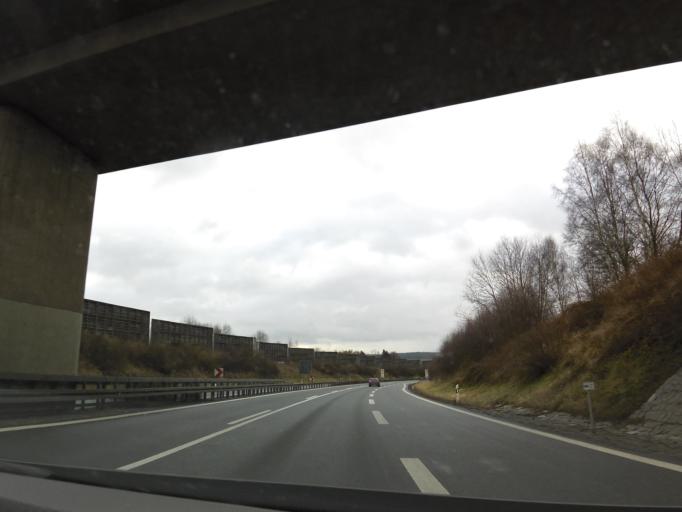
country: DE
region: Bavaria
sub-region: Upper Franconia
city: Selb
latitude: 50.1809
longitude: 12.1222
